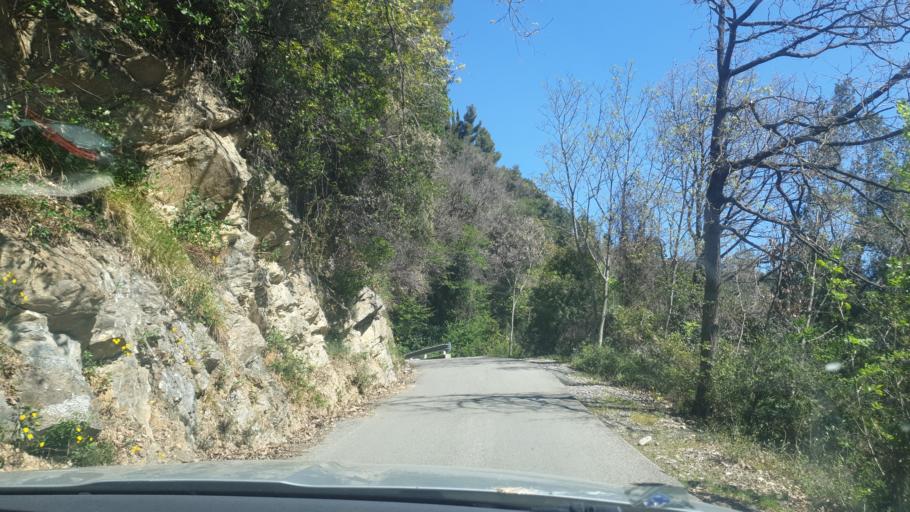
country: IT
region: Liguria
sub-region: Provincia di Genova
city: Recco
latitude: 44.3775
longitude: 9.1413
